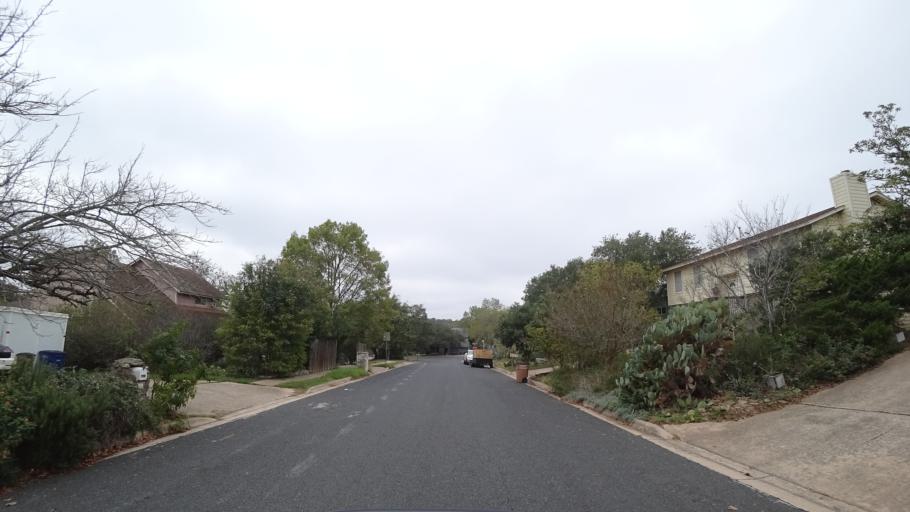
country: US
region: Texas
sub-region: Travis County
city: Barton Creek
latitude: 30.2373
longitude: -97.9005
